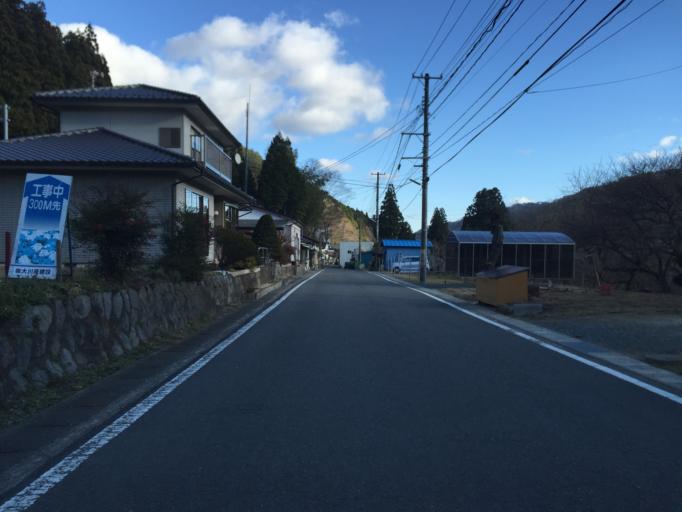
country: JP
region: Fukushima
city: Iwaki
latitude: 37.2078
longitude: 140.7482
